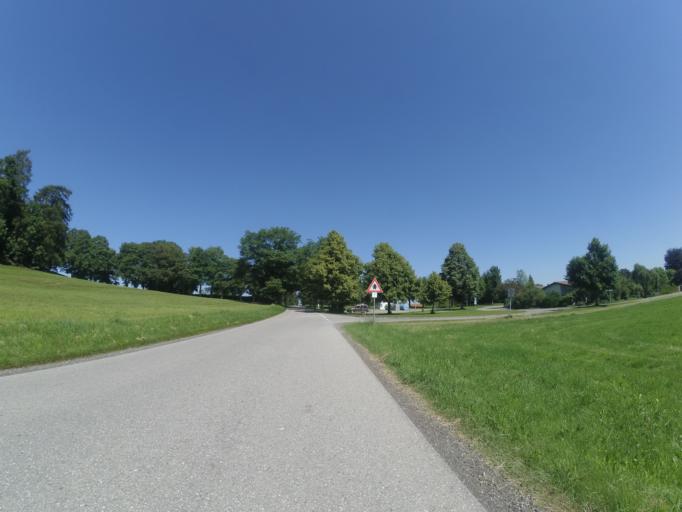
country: DE
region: Baden-Wuerttemberg
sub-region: Tuebingen Region
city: Bad Wurzach
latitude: 47.9042
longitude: 9.9021
